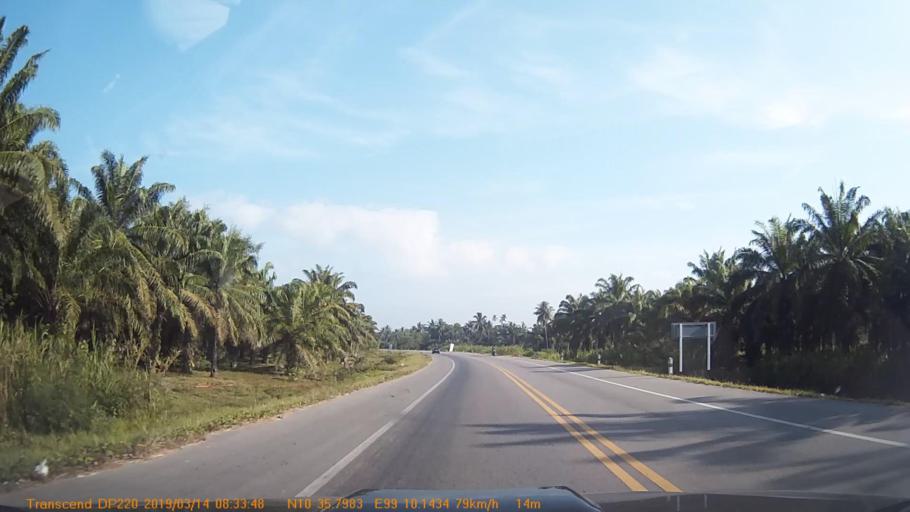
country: TH
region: Chumphon
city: Tha Sae
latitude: 10.5970
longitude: 99.1691
